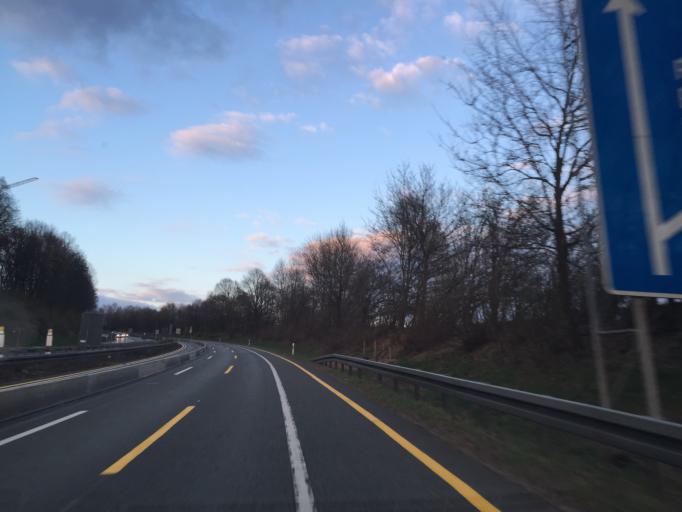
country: DE
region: Hesse
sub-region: Regierungsbezirk Kassel
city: Friedewald
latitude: 50.8887
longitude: 9.8465
